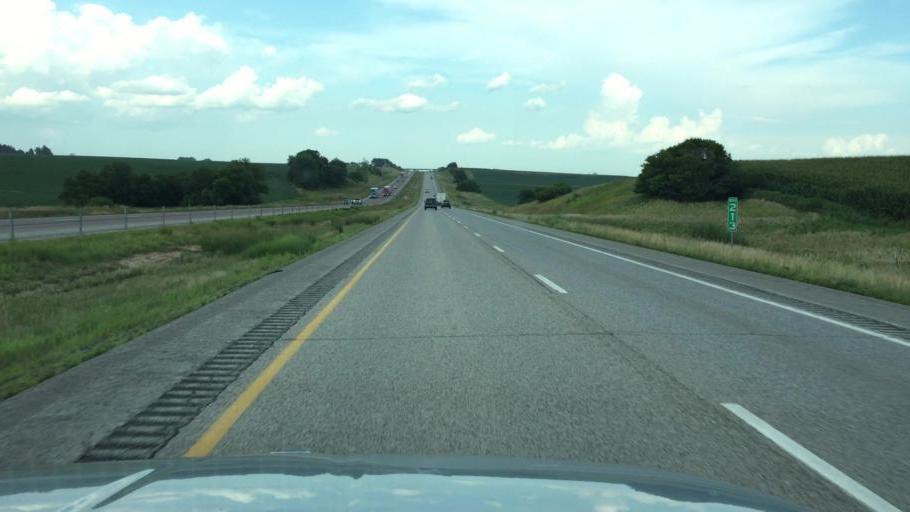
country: US
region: Iowa
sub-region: Iowa County
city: Marengo
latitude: 41.6954
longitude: -92.1415
